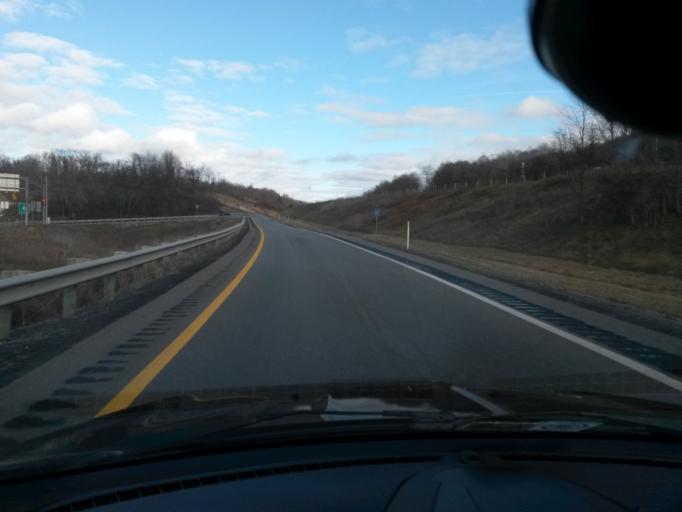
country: US
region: West Virginia
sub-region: Mercer County
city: Bluefield
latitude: 37.2718
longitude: -81.1658
